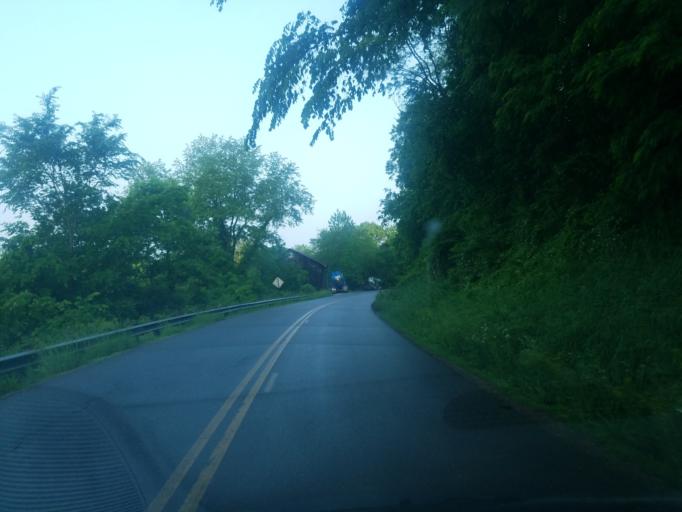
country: US
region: Ohio
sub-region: Stark County
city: Minerva
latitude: 40.6996
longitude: -81.0716
